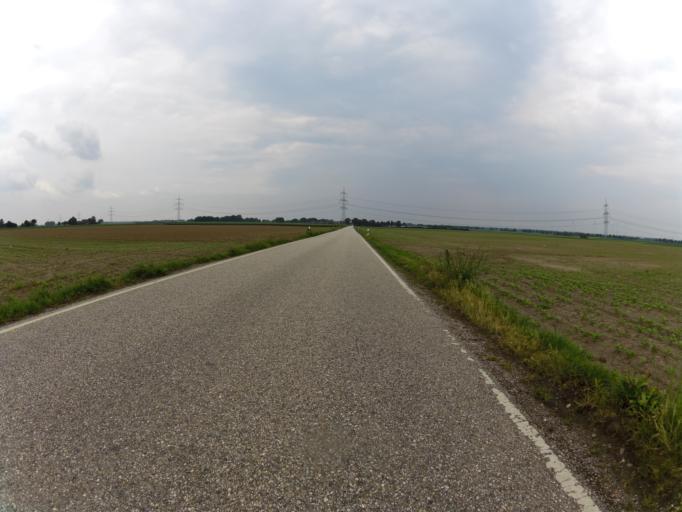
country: DE
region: North Rhine-Westphalia
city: Baesweiler
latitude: 50.9552
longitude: 6.1680
